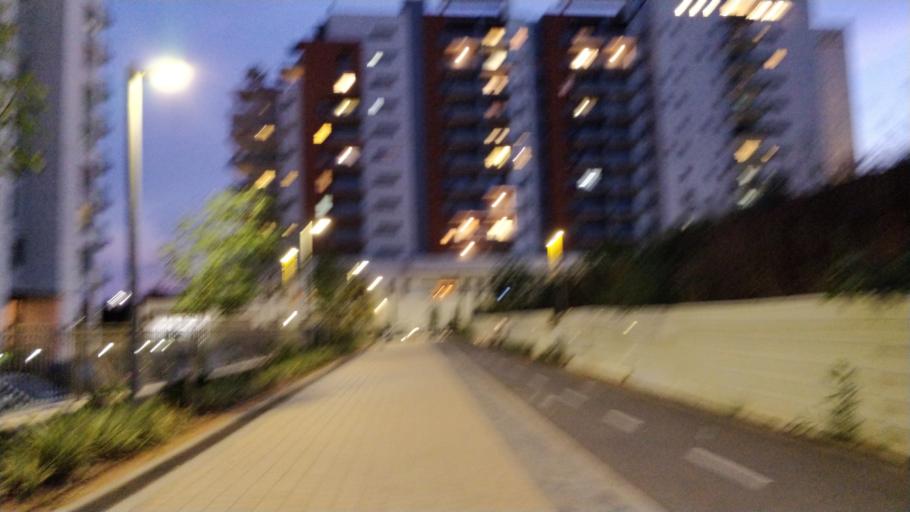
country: IL
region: Central District
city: Ganne Tiqwa
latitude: 32.0651
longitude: 34.8770
